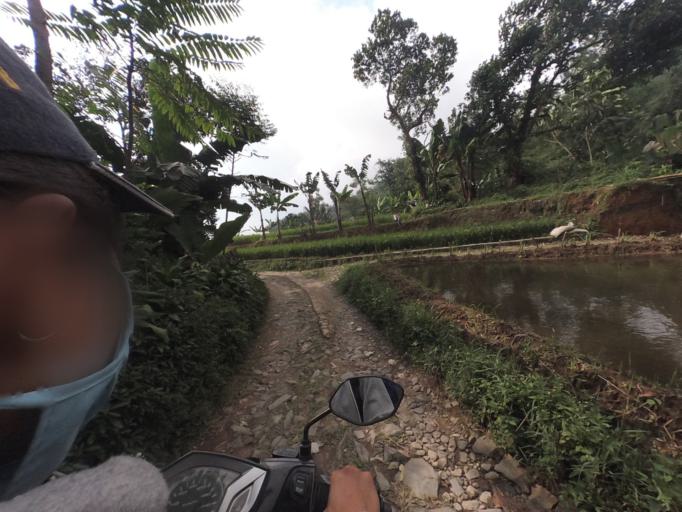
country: ID
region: West Java
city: Cicurug
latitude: -6.7043
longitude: 106.6638
